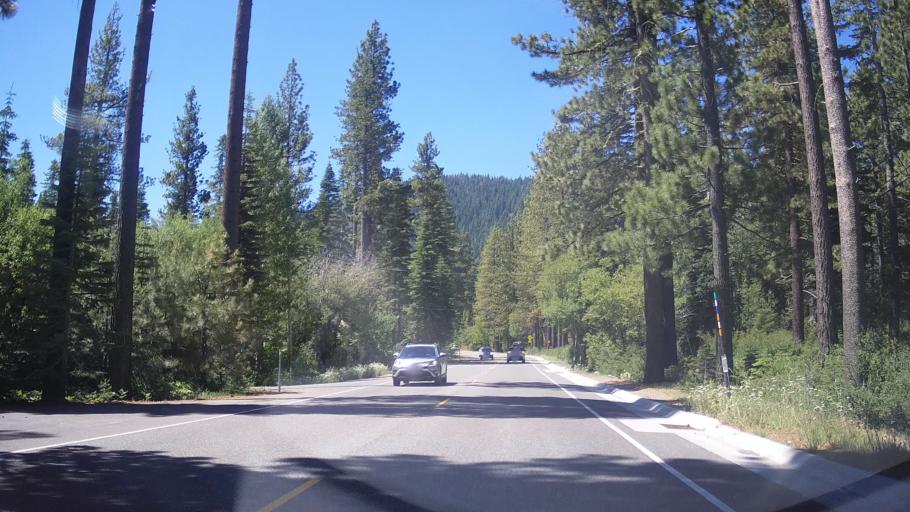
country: US
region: California
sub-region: Placer County
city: Sunnyside-Tahoe City
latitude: 39.1303
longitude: -120.1600
